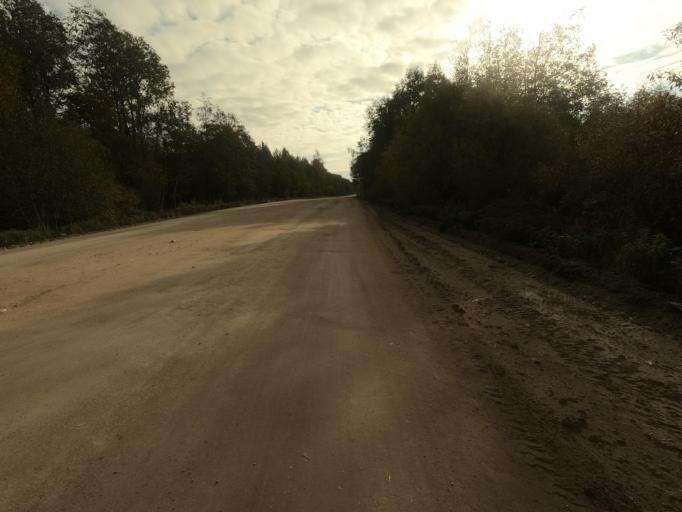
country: RU
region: Novgorod
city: Batetskiy
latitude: 58.8004
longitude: 30.6302
